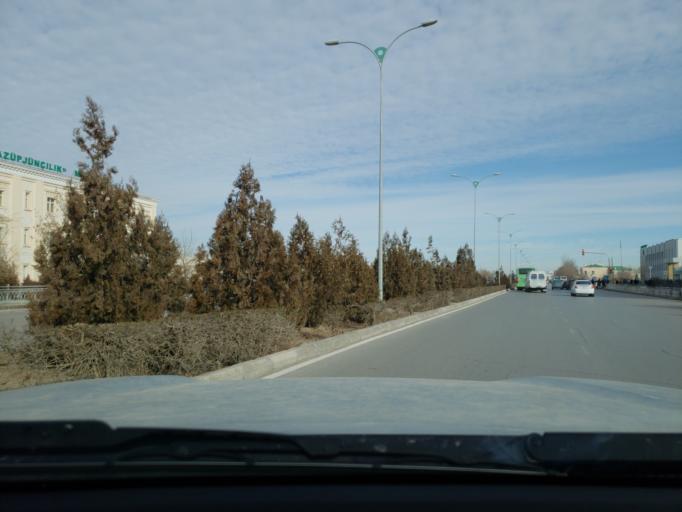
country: TM
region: Dasoguz
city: Dasoguz
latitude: 41.8471
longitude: 59.9640
